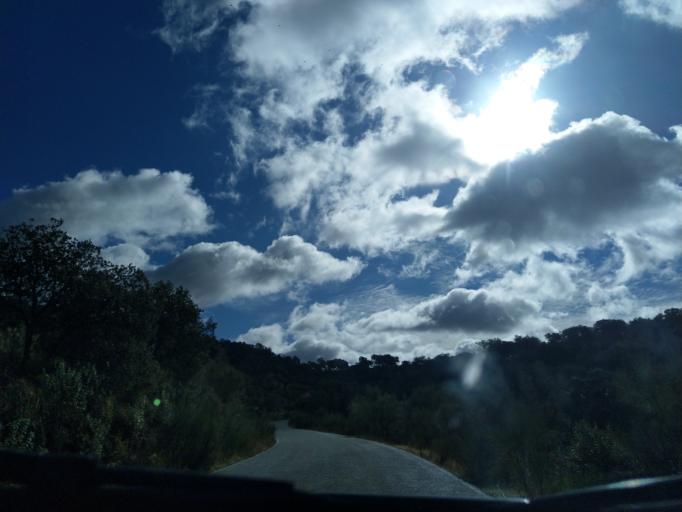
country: ES
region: Extremadura
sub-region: Provincia de Badajoz
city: Reina
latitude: 38.1321
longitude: -5.9173
